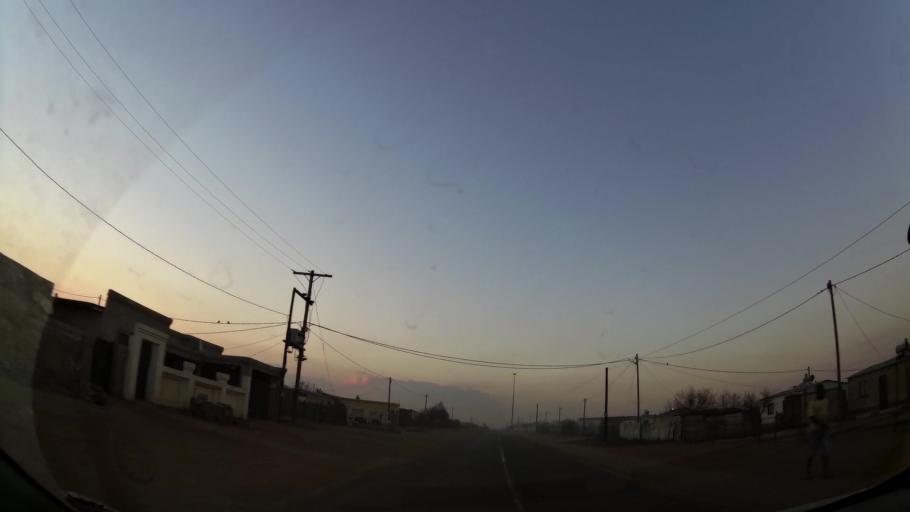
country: ZA
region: Gauteng
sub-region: Ekurhuleni Metropolitan Municipality
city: Nigel
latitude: -26.3667
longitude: 28.3935
